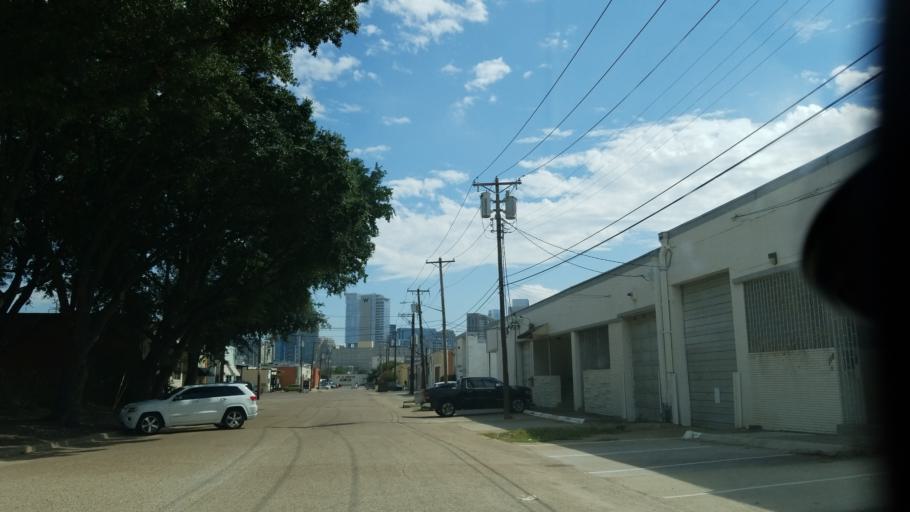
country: US
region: Texas
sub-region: Dallas County
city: Dallas
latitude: 32.7833
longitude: -96.8192
